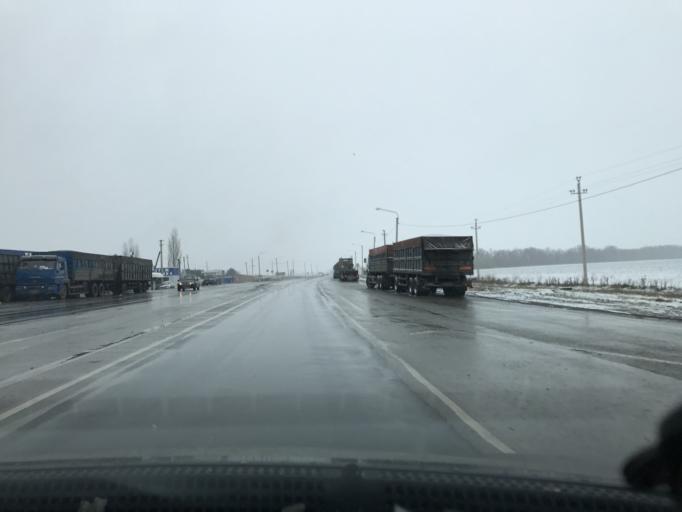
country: RU
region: Rostov
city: Yegorlykskaya
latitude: 46.5515
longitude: 40.6486
